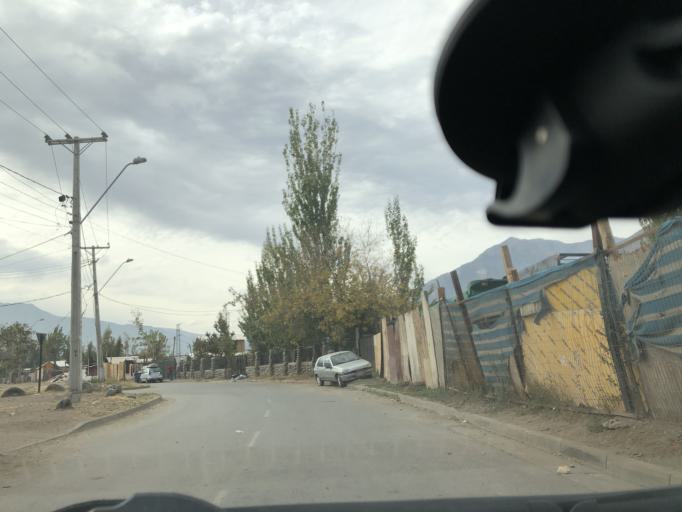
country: CL
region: Santiago Metropolitan
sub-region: Provincia de Cordillera
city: Puente Alto
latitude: -33.6146
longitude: -70.5211
